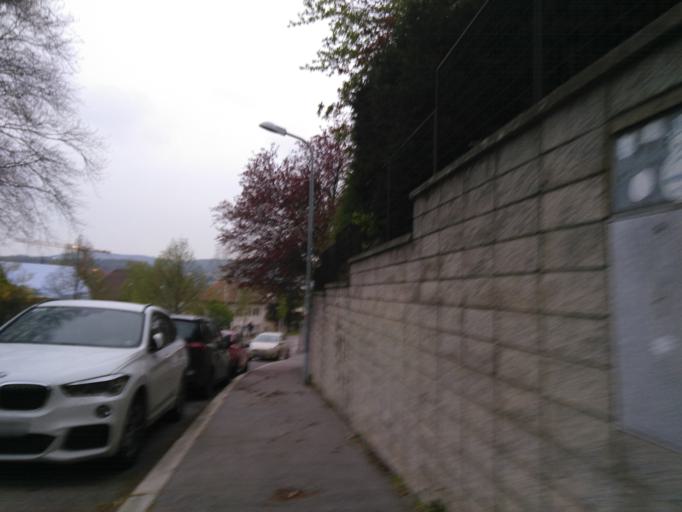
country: AT
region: Lower Austria
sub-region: Politischer Bezirk Modling
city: Perchtoldsdorf
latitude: 48.1744
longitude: 16.2906
